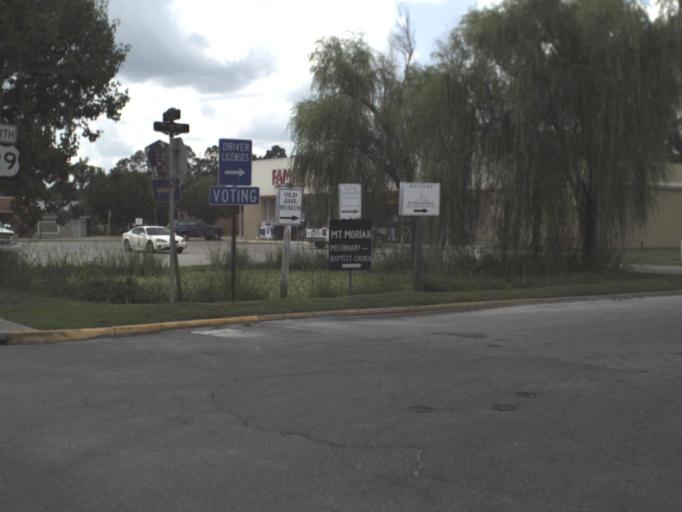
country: US
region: Florida
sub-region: Hamilton County
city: Jasper
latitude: 30.5181
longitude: -82.9466
